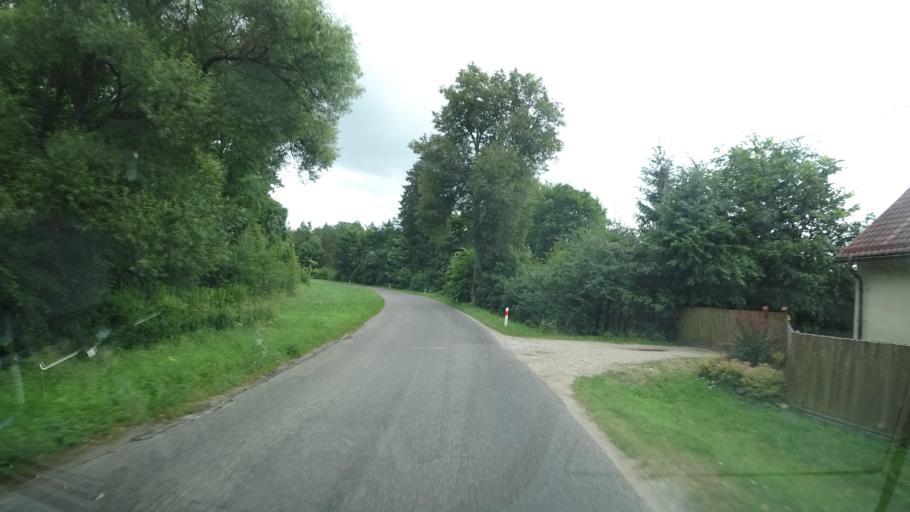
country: PL
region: Warmian-Masurian Voivodeship
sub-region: Powiat goldapski
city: Goldap
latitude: 54.3104
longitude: 22.3732
